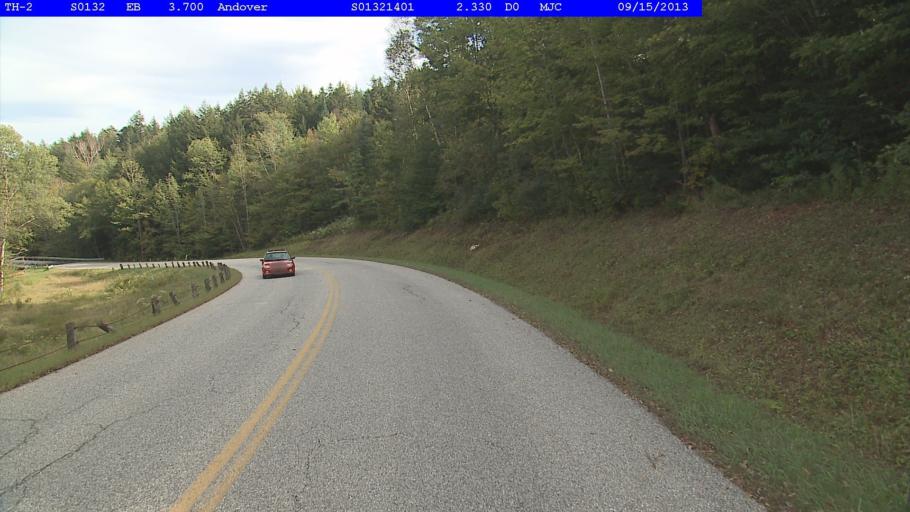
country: US
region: Vermont
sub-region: Windsor County
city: Chester
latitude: 43.2859
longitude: -72.7253
